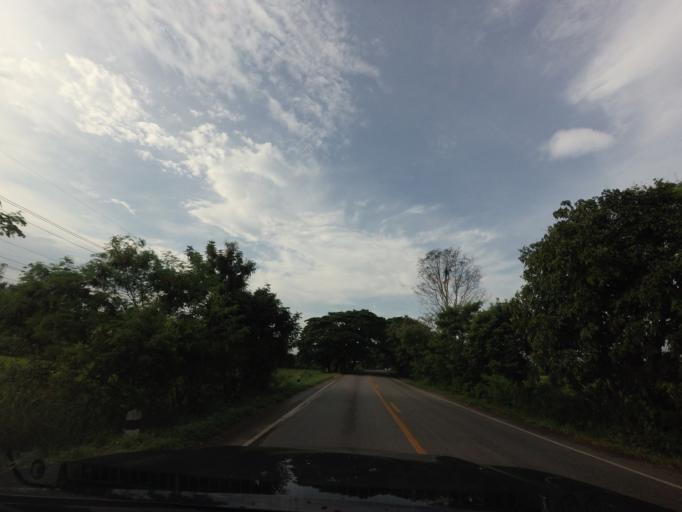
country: TH
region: Changwat Udon Thani
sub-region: Amphoe Ban Phue
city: Ban Phue
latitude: 17.7551
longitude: 102.3980
